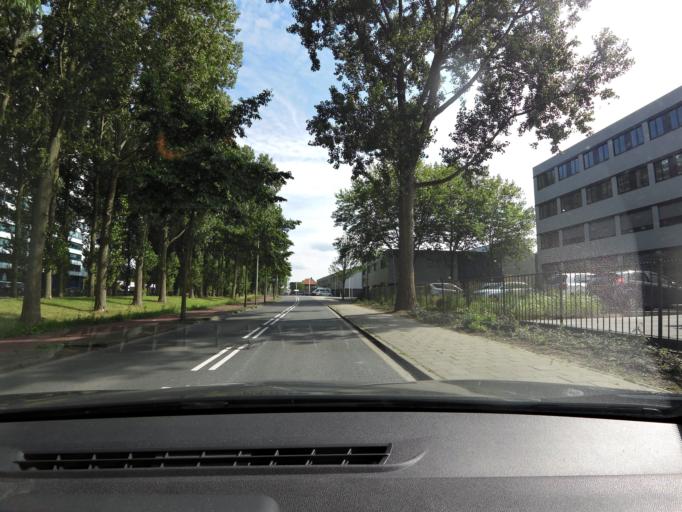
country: NL
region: South Holland
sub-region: Gemeente Delft
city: Delft
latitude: 51.9906
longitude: 4.3739
